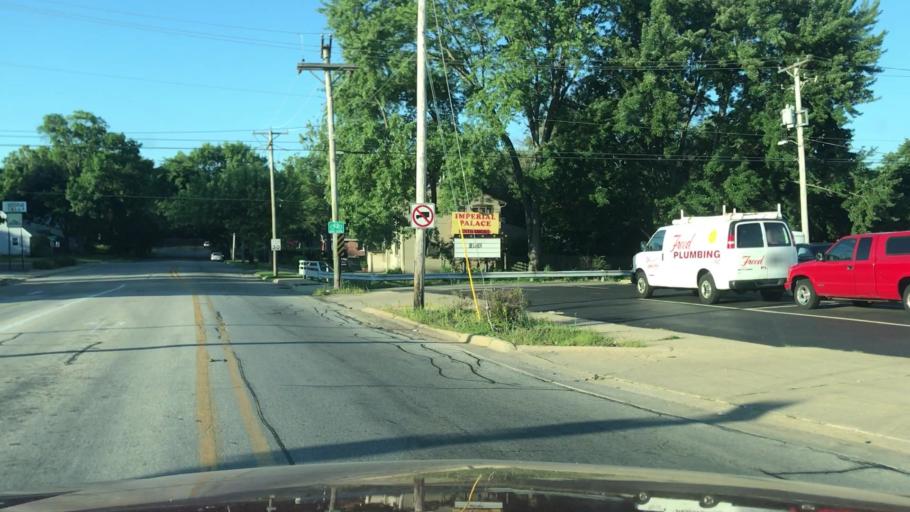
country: US
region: Illinois
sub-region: Winnebago County
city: Rockford
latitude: 42.2659
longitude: -89.0425
